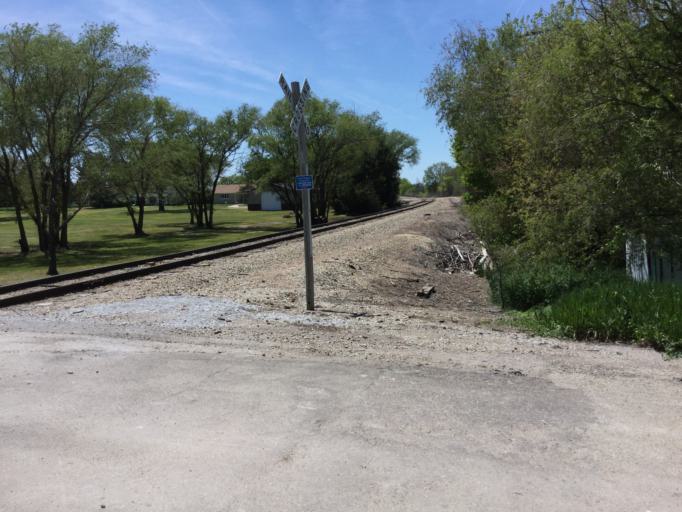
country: US
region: Kansas
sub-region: Smith County
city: Smith Center
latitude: 39.7745
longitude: -98.7889
